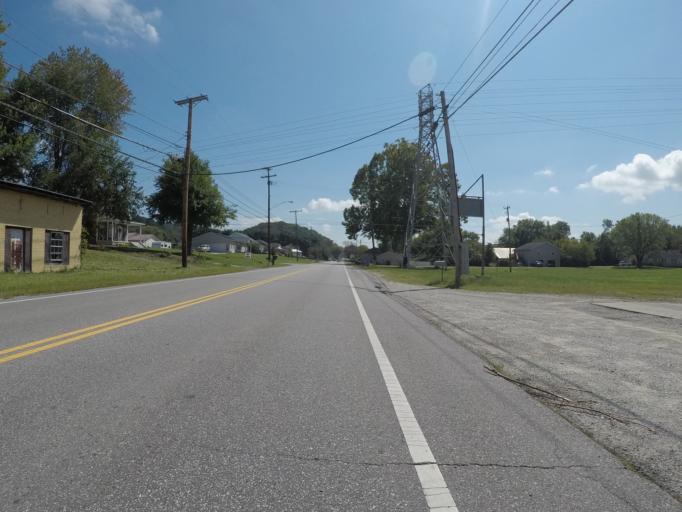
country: US
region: Ohio
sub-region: Lawrence County
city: South Point
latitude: 38.4119
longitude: -82.5784
